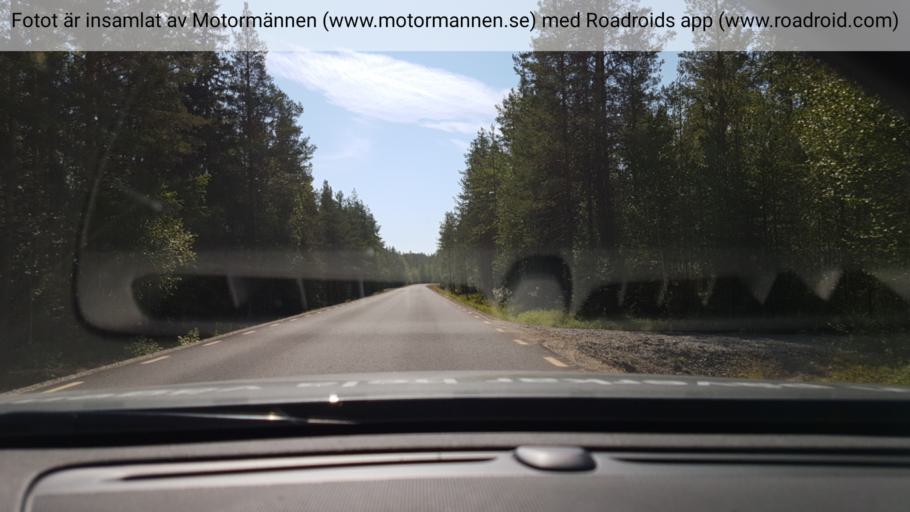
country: SE
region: Vaesterbotten
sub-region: Norsjo Kommun
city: Norsjoe
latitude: 64.4726
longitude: 19.3259
